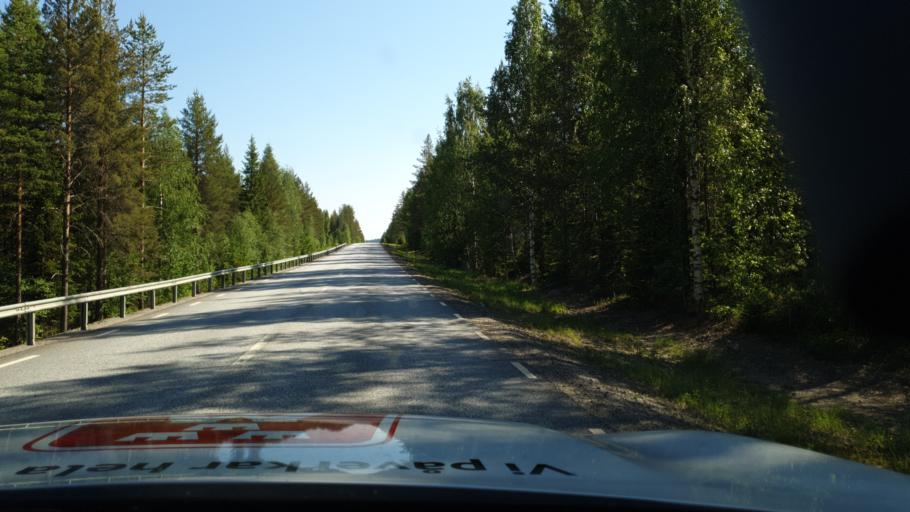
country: SE
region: Vaesterbotten
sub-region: Umea Kommun
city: Ersmark
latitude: 64.2841
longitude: 20.2228
